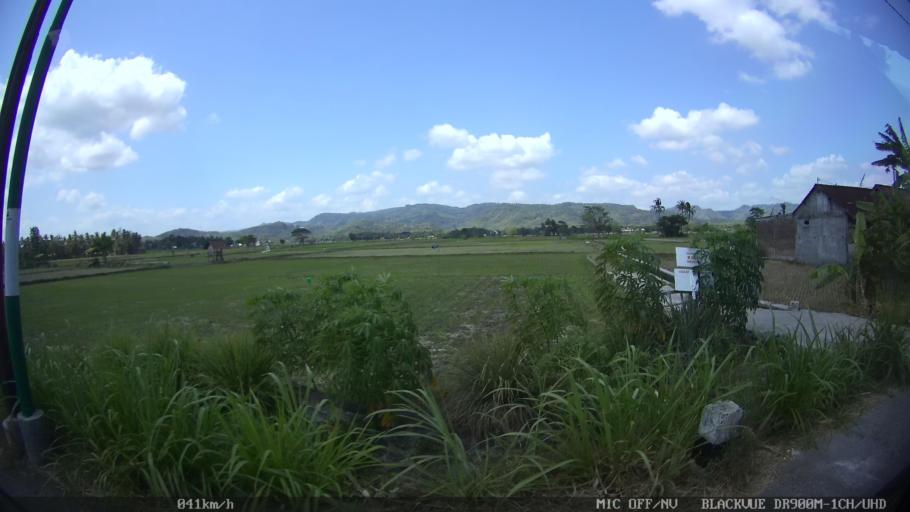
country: ID
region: Daerah Istimewa Yogyakarta
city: Pundong
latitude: -7.9296
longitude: 110.3736
